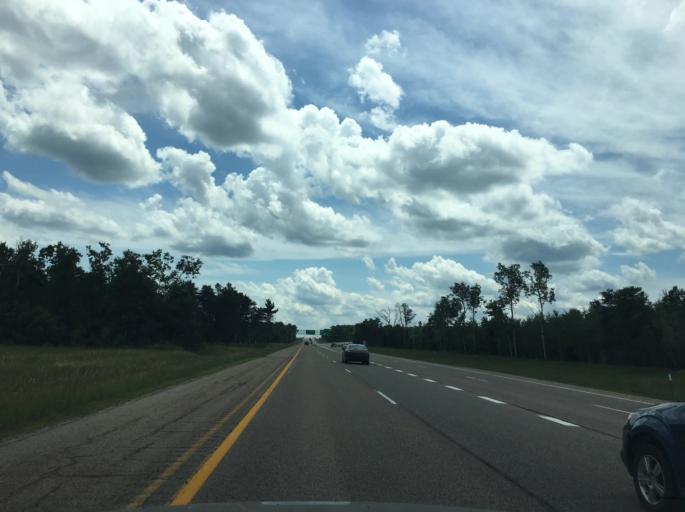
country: US
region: Michigan
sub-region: Crawford County
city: Grayling
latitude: 44.5878
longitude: -84.7097
